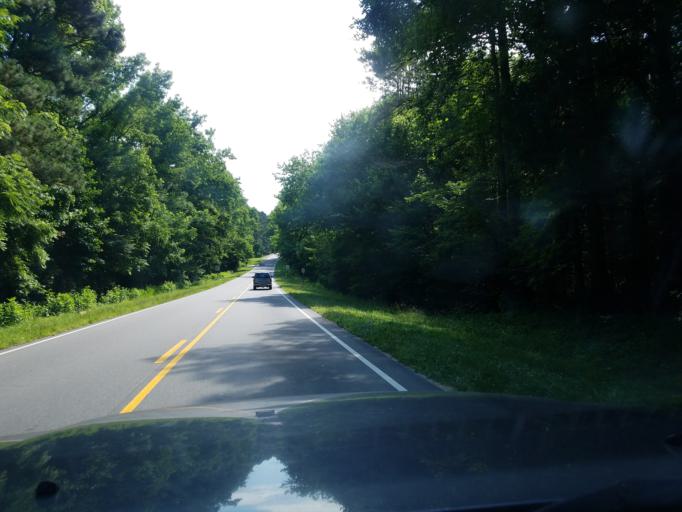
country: US
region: North Carolina
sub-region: Vance County
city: South Henderson
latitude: 36.3339
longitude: -78.4651
